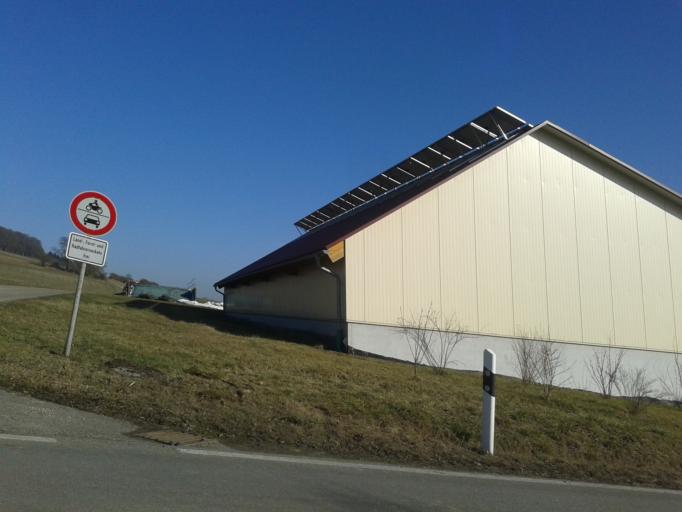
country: DE
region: Baden-Wuerttemberg
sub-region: Tuebingen Region
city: Erbach
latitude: 48.3741
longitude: 9.9109
